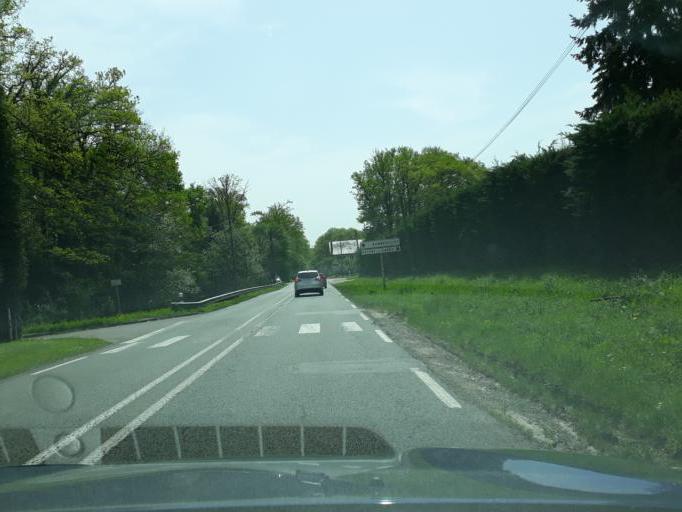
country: FR
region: Ile-de-France
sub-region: Departement des Yvelines
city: Saint-Leger-en-Yvelines
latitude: 48.6952
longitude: 1.7709
